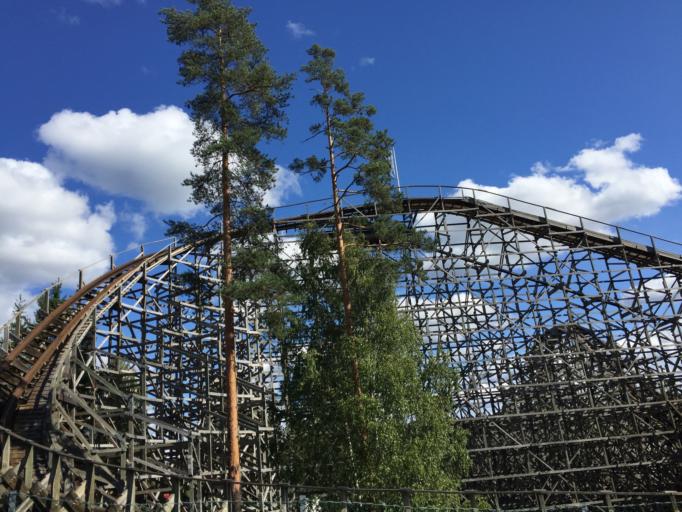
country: NO
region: Akershus
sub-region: Ski
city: Ski
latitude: 59.7475
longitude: 10.7758
